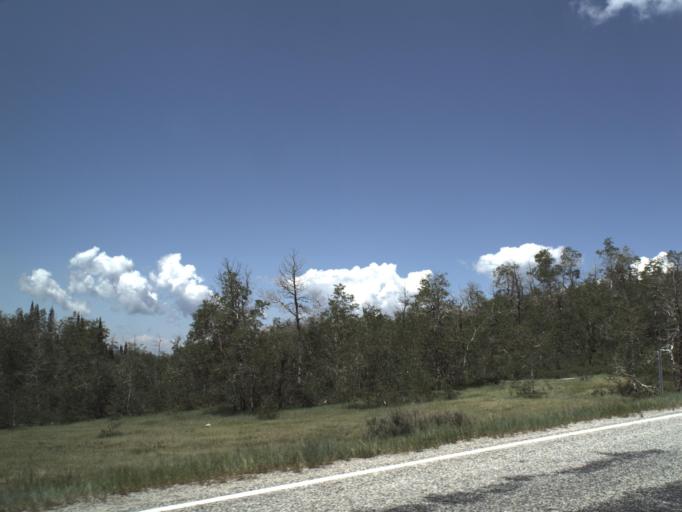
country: US
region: Utah
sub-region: Weber County
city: Wolf Creek
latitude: 41.4066
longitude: -111.5394
